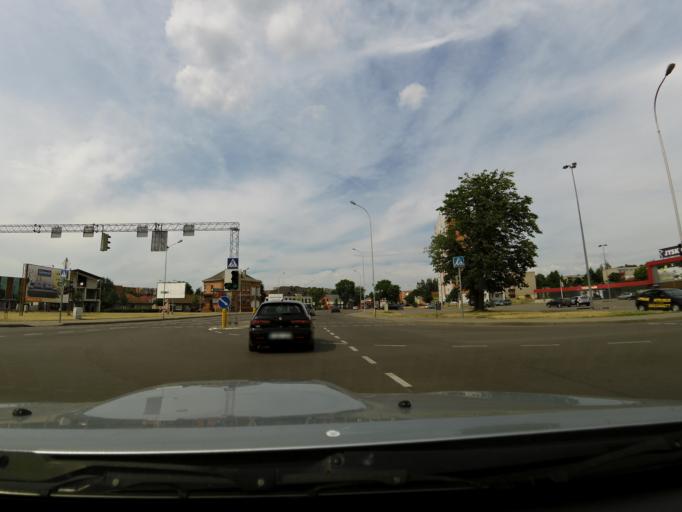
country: LT
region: Marijampoles apskritis
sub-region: Marijampole Municipality
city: Marijampole
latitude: 54.5607
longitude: 23.3533
